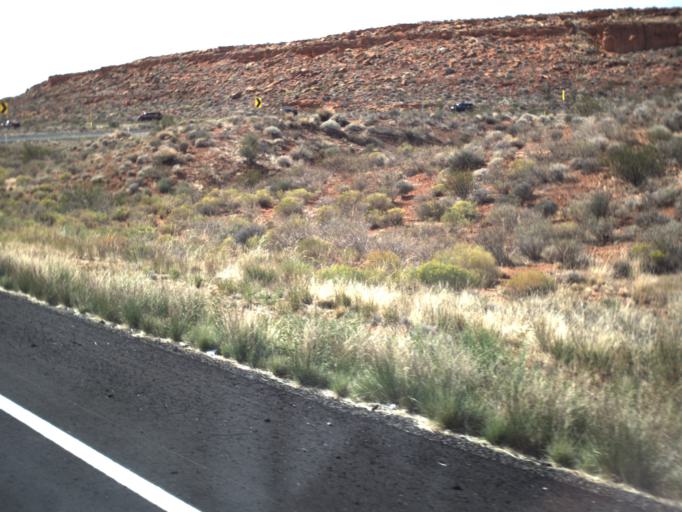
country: US
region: Utah
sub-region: Washington County
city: Washington
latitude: 37.1667
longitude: -113.4523
